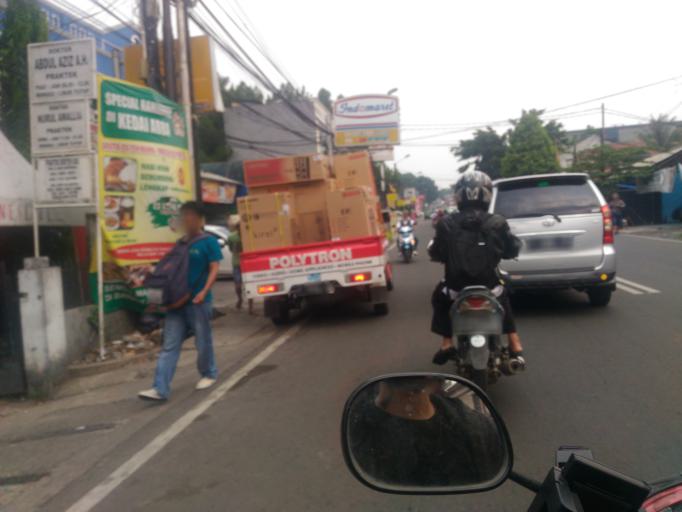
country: ID
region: West Java
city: Caringin
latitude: -6.6428
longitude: 106.8380
